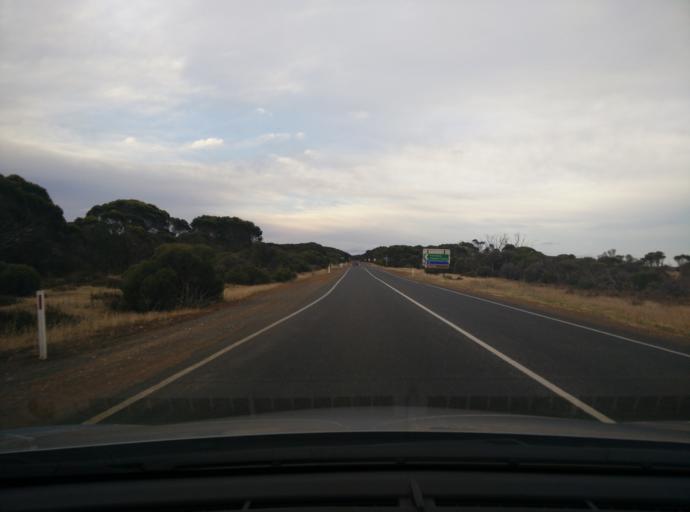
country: AU
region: South Australia
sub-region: Kangaroo Island
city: Kingscote
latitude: -35.7266
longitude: 137.5605
